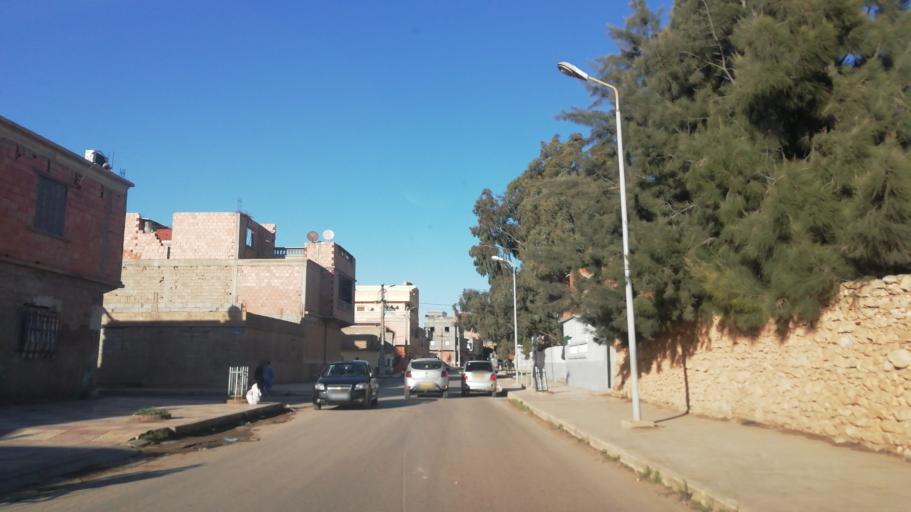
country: DZ
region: Oran
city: Sidi ech Chahmi
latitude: 35.6892
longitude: -0.4962
